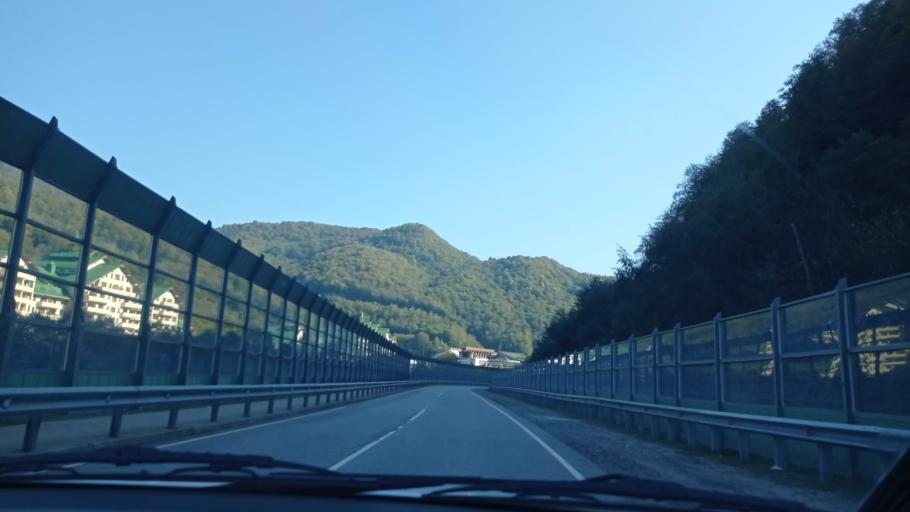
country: RU
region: Krasnodarskiy
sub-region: Sochi City
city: Krasnaya Polyana
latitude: 43.6910
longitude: 40.2719
